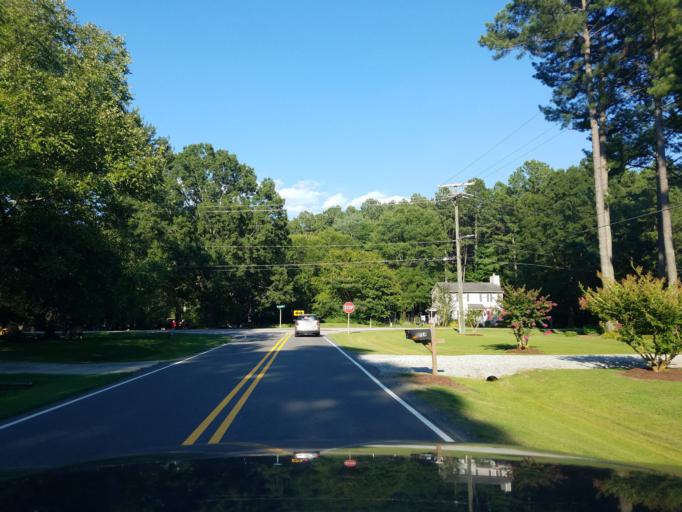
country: US
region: North Carolina
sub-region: Wake County
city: Green Level
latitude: 35.8759
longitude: -78.9155
